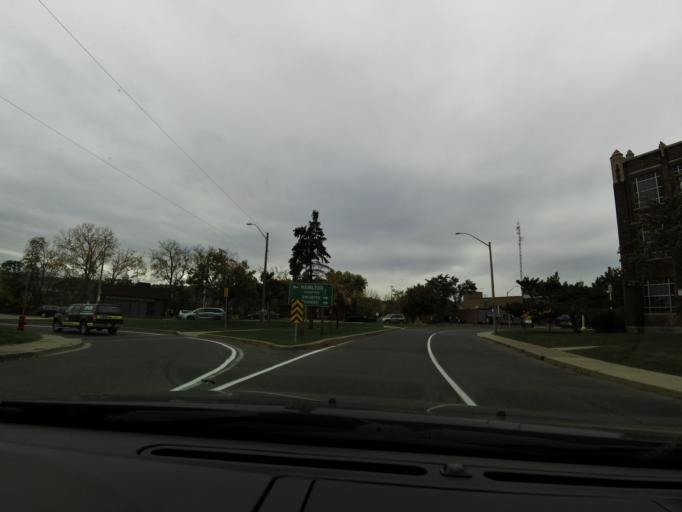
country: CA
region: Ontario
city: Hamilton
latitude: 43.2599
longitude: -79.8999
